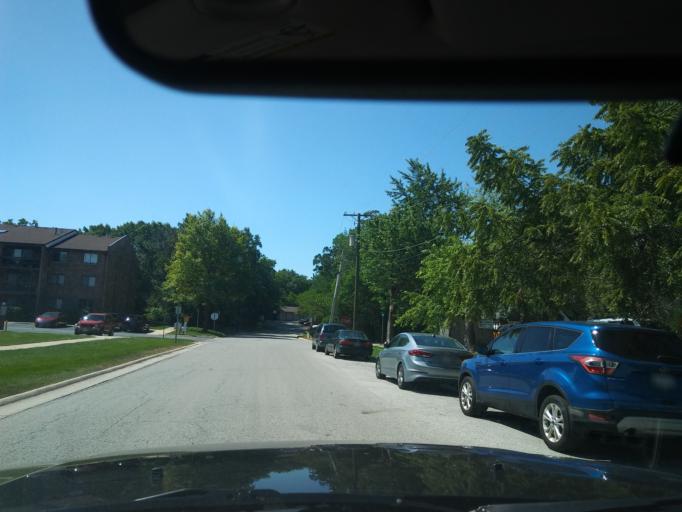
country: US
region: Illinois
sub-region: Cook County
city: Oak Forest
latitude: 41.6017
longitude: -87.7437
